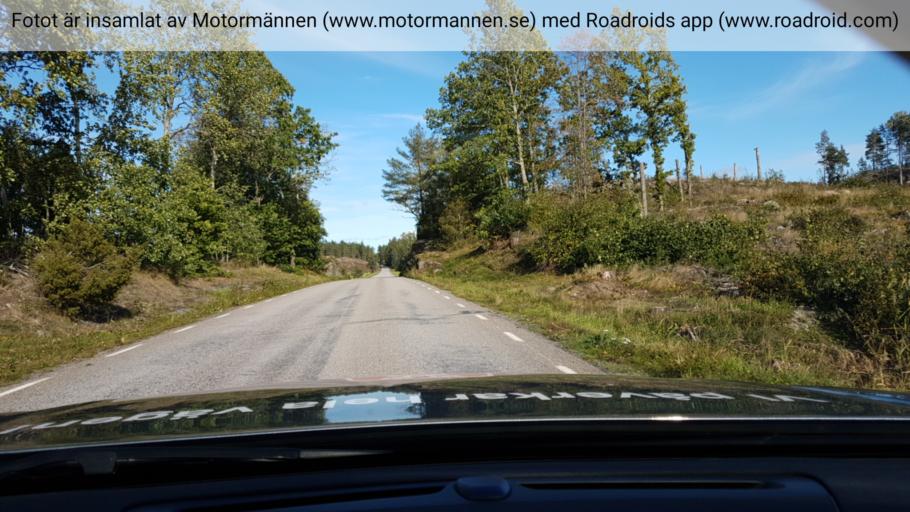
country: SE
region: OEstergoetland
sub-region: Valdemarsviks Kommun
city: Valdemarsvik
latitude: 58.0584
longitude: 16.6247
